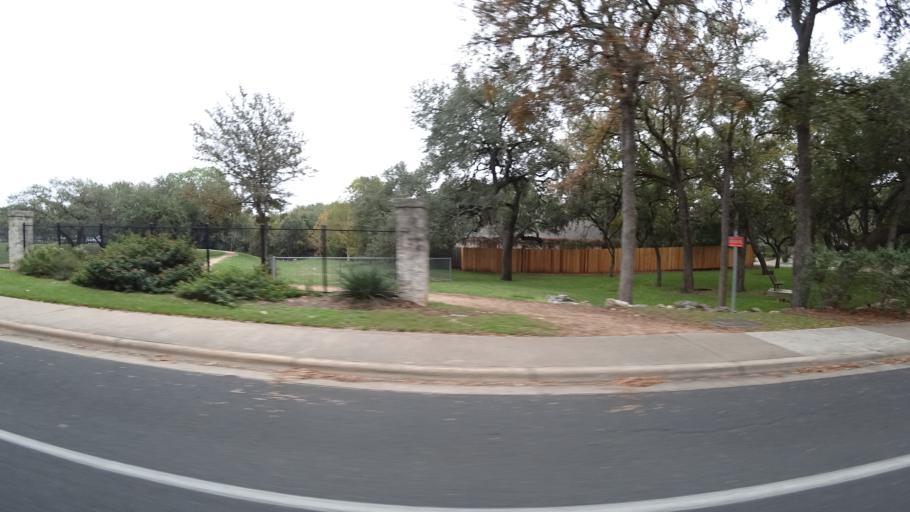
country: US
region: Texas
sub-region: Travis County
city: Shady Hollow
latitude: 30.1930
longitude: -97.8872
